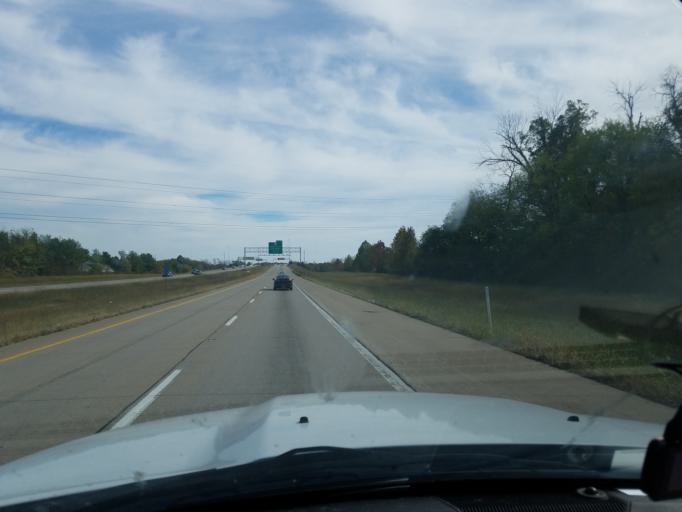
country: US
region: Indiana
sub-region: Clark County
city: Oak Park
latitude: 38.3471
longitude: -85.7253
